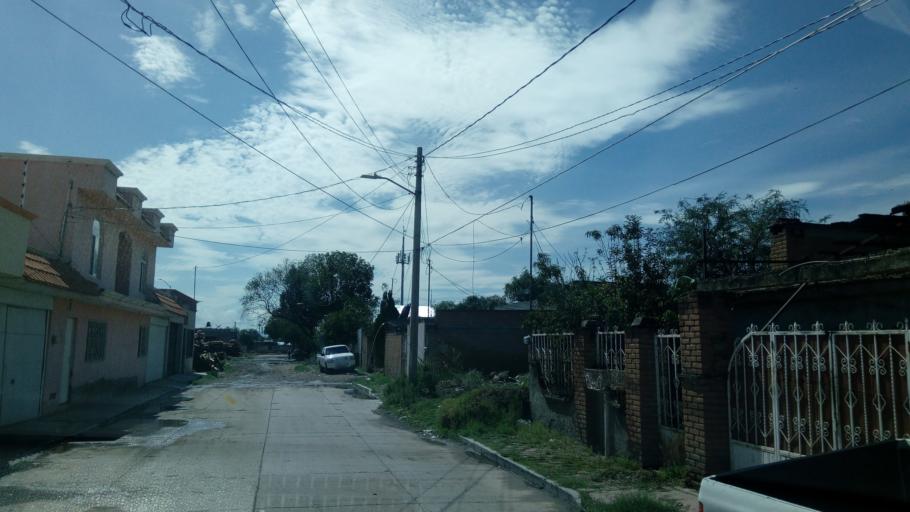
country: MX
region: Durango
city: Victoria de Durango
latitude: 23.9942
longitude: -104.6840
